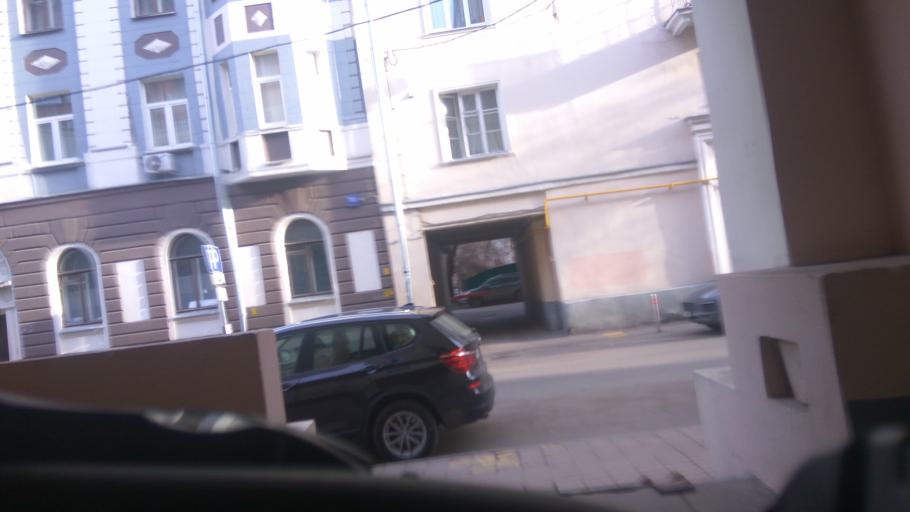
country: RU
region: Moscow
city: Taganskiy
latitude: 55.7636
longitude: 37.6508
